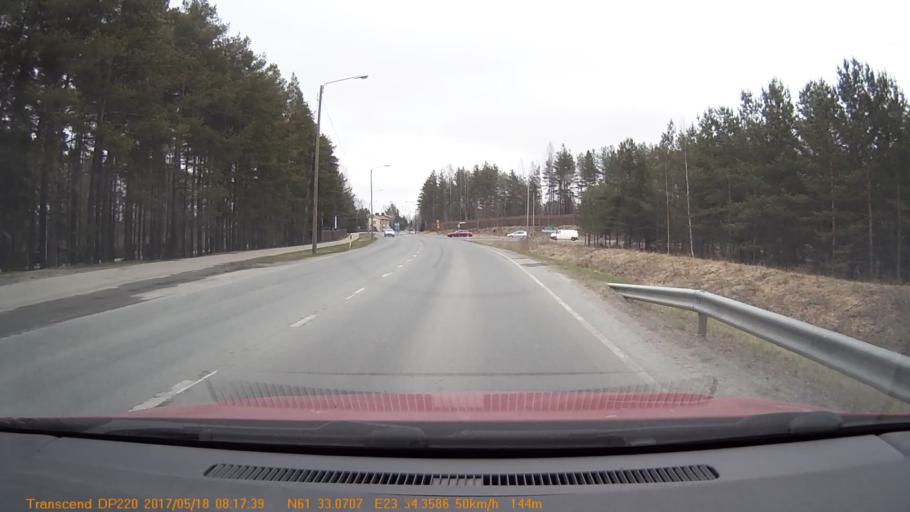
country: FI
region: Pirkanmaa
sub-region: Tampere
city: Yloejaervi
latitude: 61.5512
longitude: 23.5730
